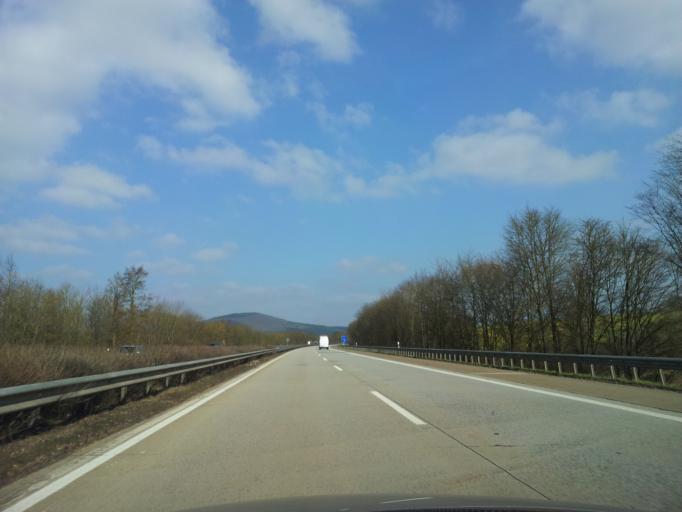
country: DE
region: Rheinland-Pfalz
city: Esch
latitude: 49.9147
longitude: 6.8552
